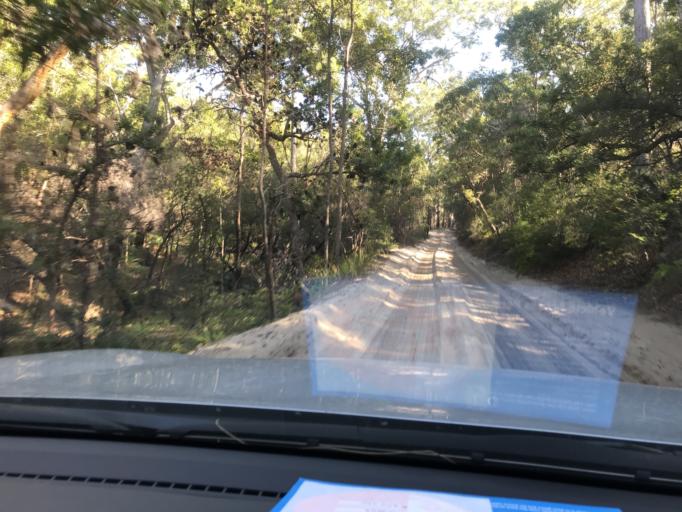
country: AU
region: Queensland
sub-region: Fraser Coast
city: Urangan
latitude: -25.5035
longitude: 153.1083
